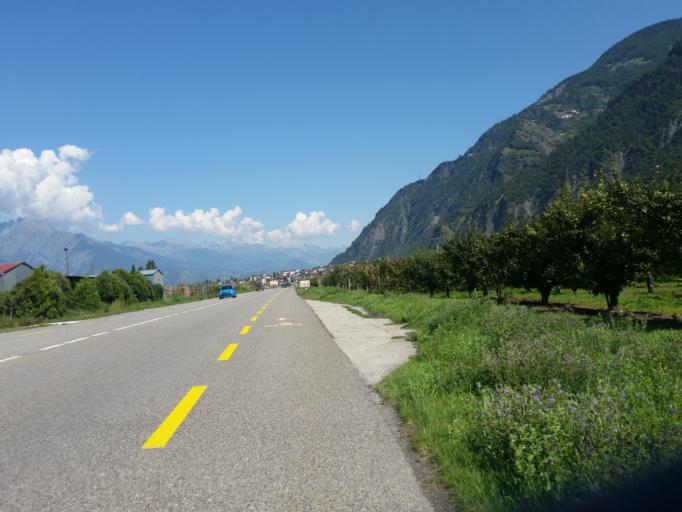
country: CH
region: Valais
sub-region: Martigny District
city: Saillon
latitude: 46.1614
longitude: 7.1999
